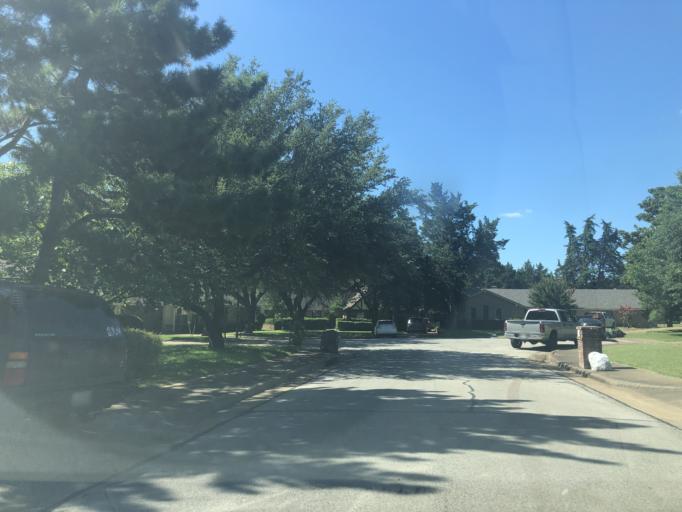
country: US
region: Texas
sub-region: Dallas County
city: Duncanville
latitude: 32.6464
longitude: -96.9397
